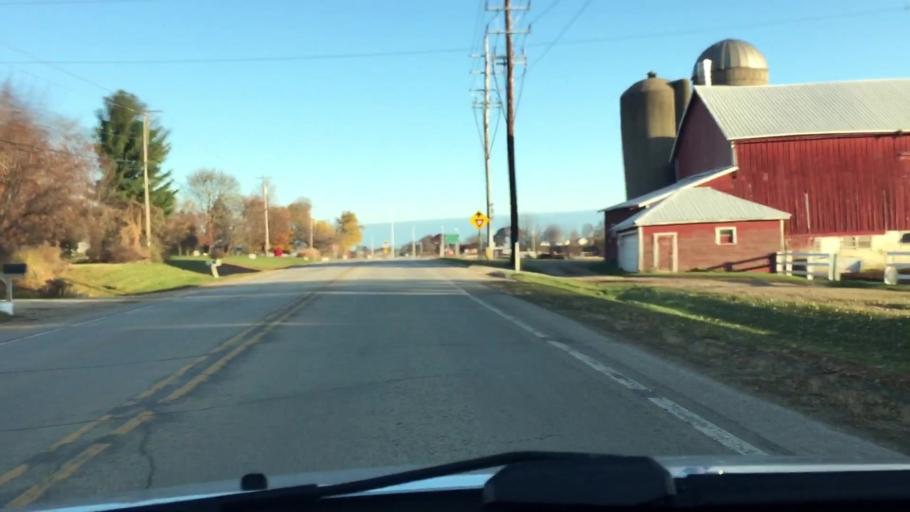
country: US
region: Wisconsin
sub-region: Washington County
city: Hartford
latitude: 43.3227
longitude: -88.4590
